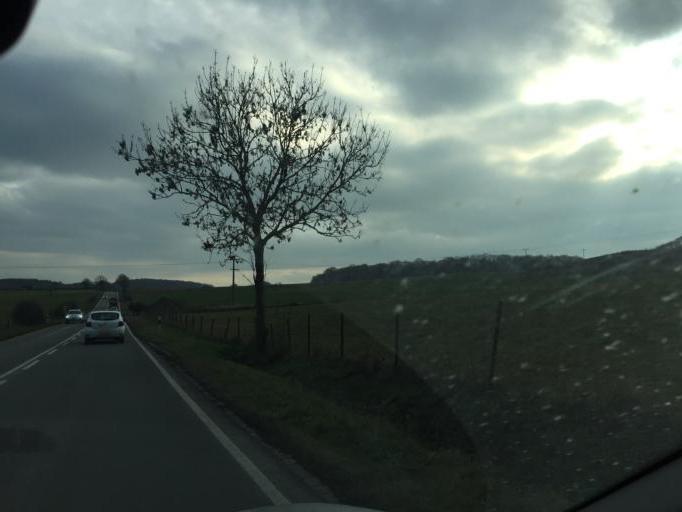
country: LU
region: Diekirch
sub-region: Canton de Redange
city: Useldange
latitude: 49.7543
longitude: 5.9622
